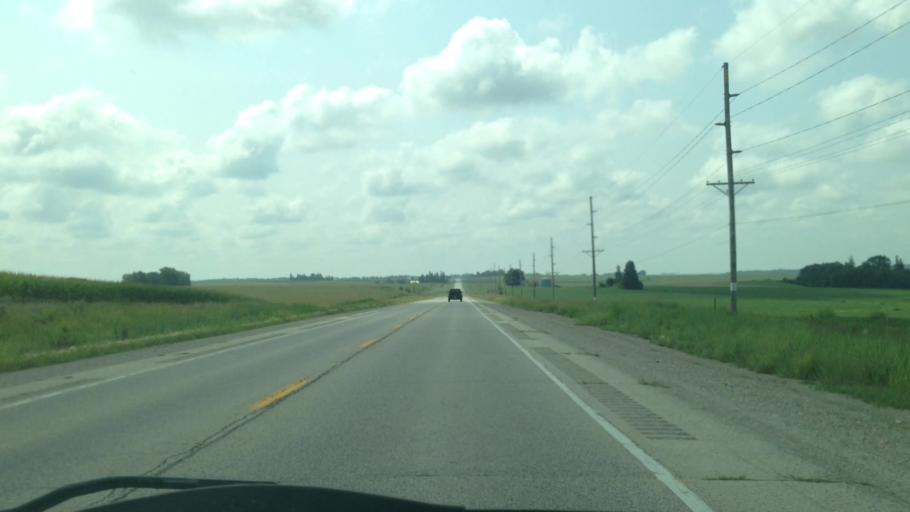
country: US
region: Iowa
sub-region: Benton County
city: Walford
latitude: 41.8688
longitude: -91.8703
